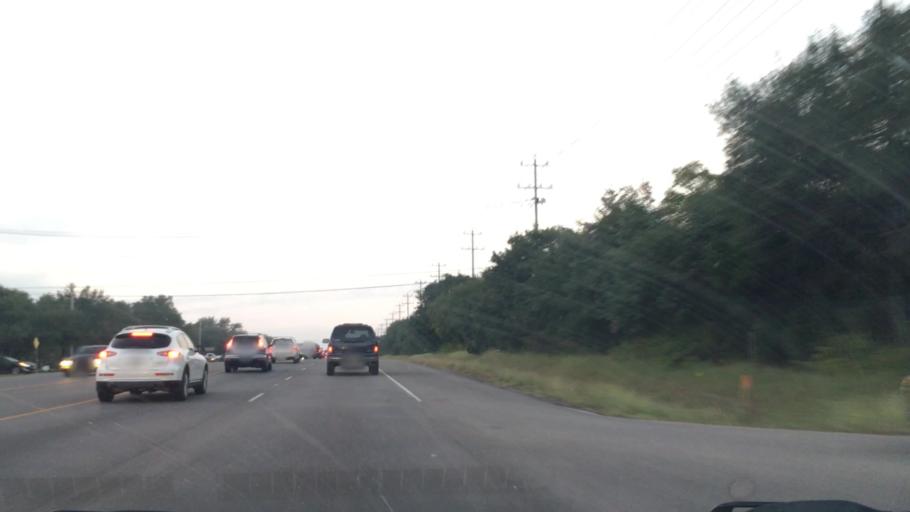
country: US
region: Texas
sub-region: Williamson County
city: Anderson Mill
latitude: 30.4123
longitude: -97.8497
